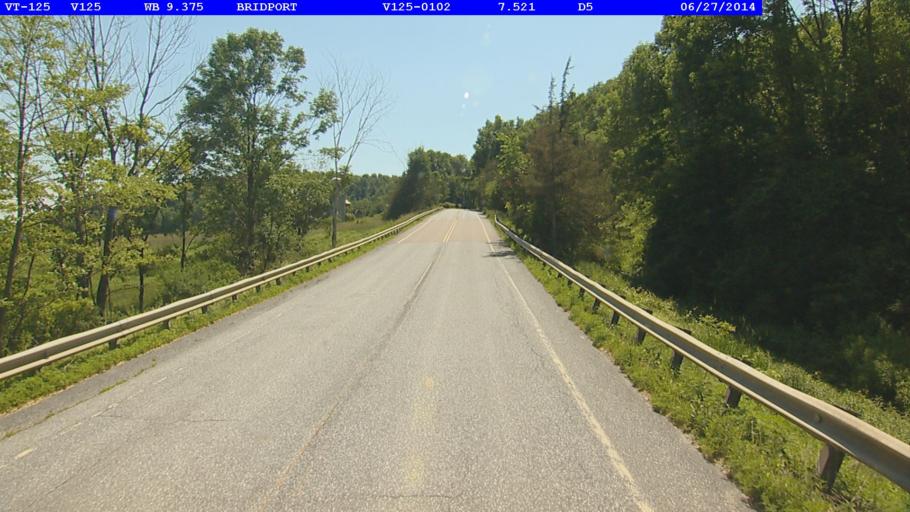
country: US
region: Vermont
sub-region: Addison County
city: Middlebury (village)
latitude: 43.9944
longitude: -73.2699
